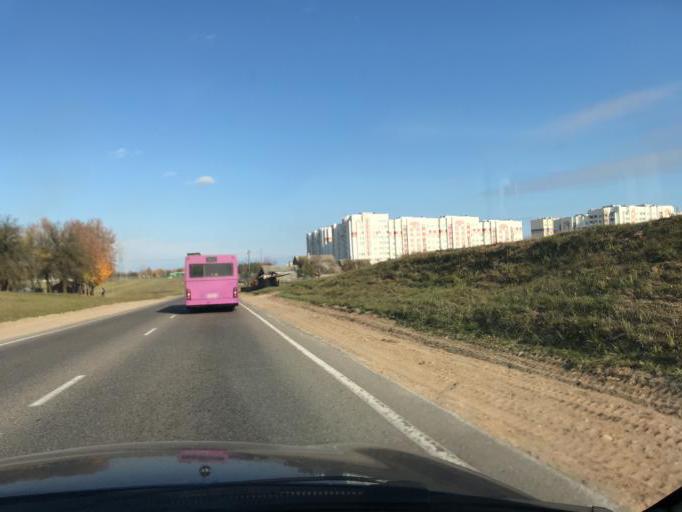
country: BY
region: Grodnenskaya
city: Lida
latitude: 53.9017
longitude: 25.2508
